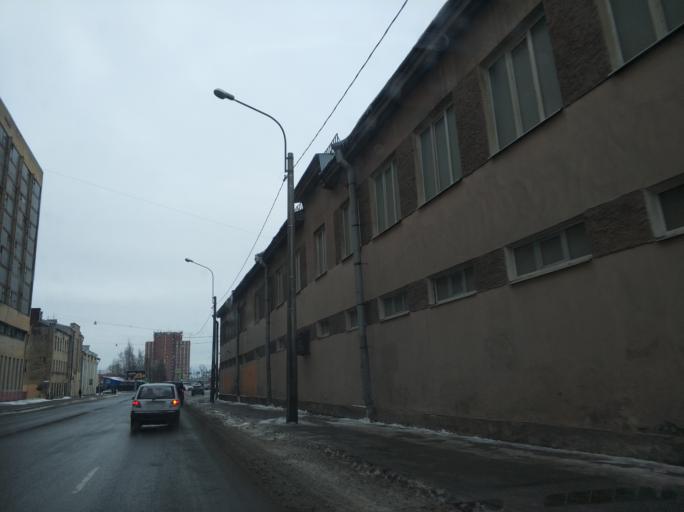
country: RU
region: St.-Petersburg
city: Centralniy
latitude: 59.9183
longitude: 30.3741
